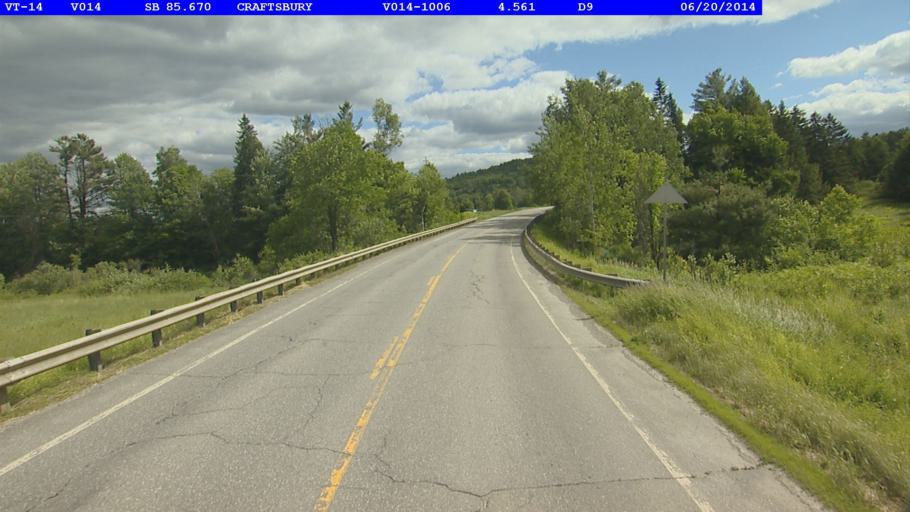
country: US
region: Vermont
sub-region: Caledonia County
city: Hardwick
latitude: 44.6563
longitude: -72.4041
